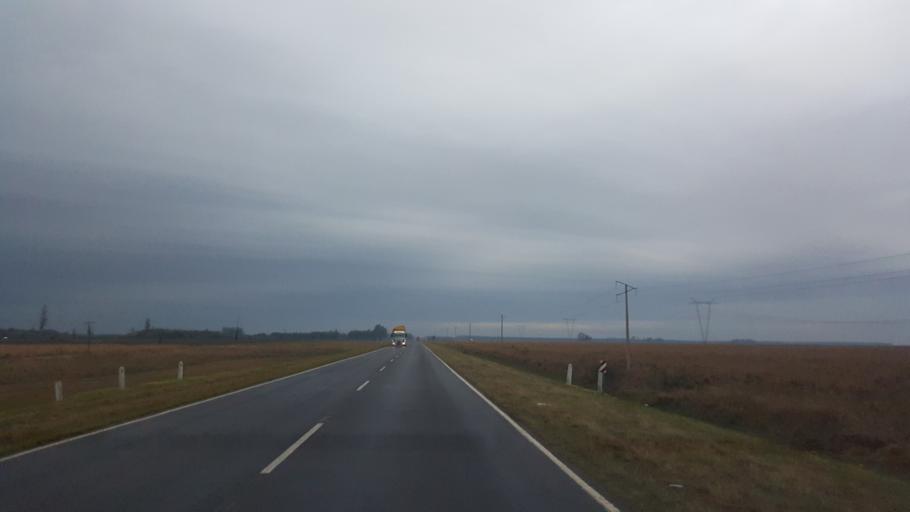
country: AR
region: Corrientes
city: Ituzaingo
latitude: -27.5917
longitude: -56.4764
